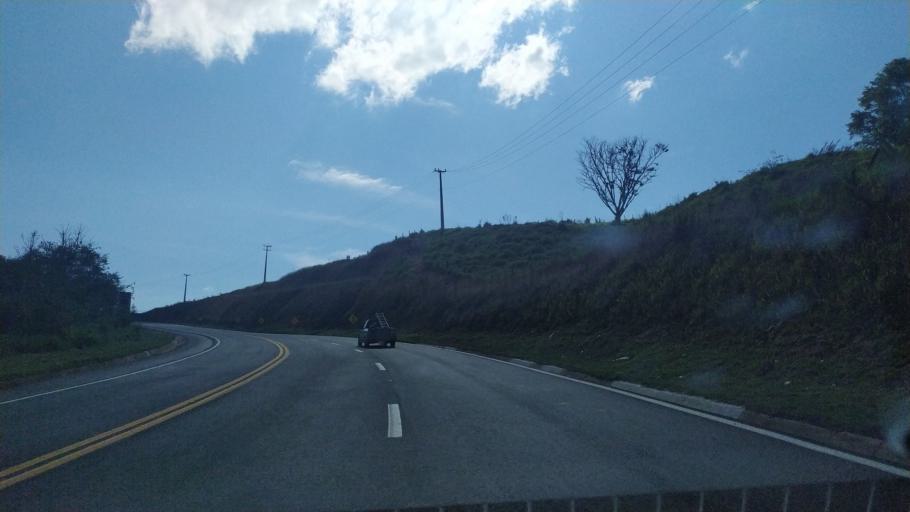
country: BR
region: Parana
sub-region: Telemaco Borba
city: Telemaco Borba
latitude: -24.2874
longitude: -50.7045
